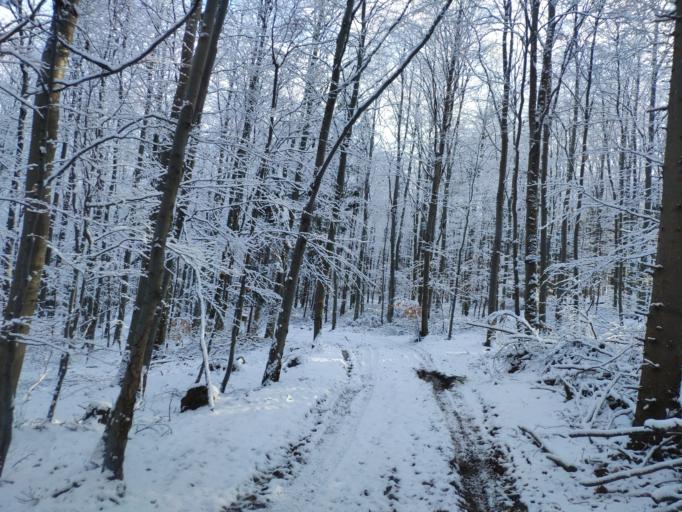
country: SK
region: Kosicky
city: Moldava nad Bodvou
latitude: 48.7469
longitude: 21.0845
